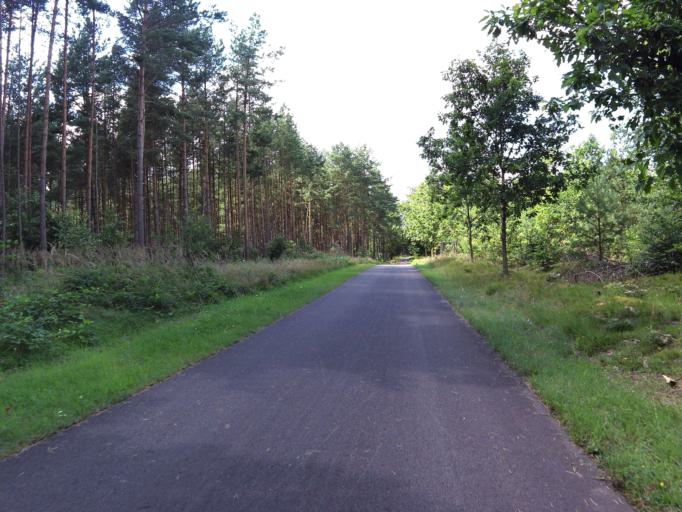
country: DE
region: Brandenburg
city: Lychen
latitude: 53.1719
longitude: 13.3706
